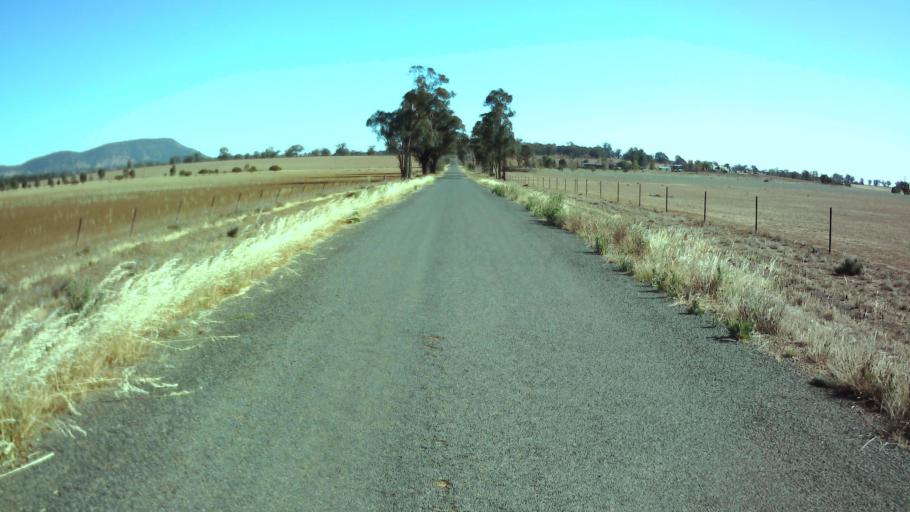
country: AU
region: New South Wales
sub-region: Weddin
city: Grenfell
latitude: -33.7970
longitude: 147.9564
